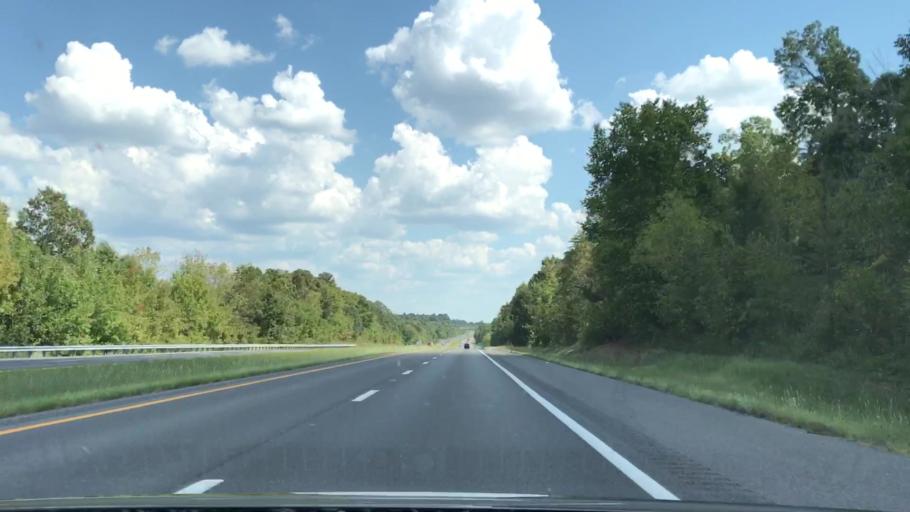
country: US
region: Kentucky
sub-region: Lyon County
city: Eddyville
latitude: 37.1096
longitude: -88.0179
